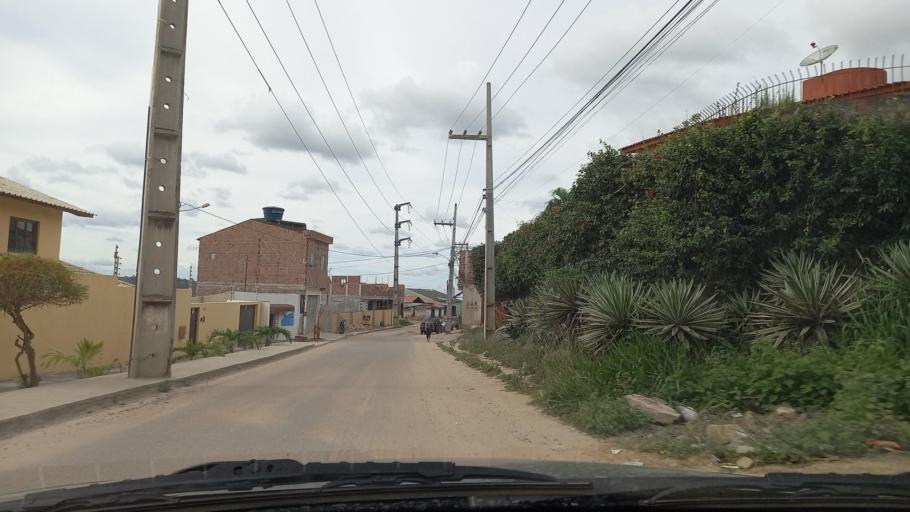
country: BR
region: Pernambuco
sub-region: Gravata
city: Gravata
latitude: -8.2105
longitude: -35.5763
